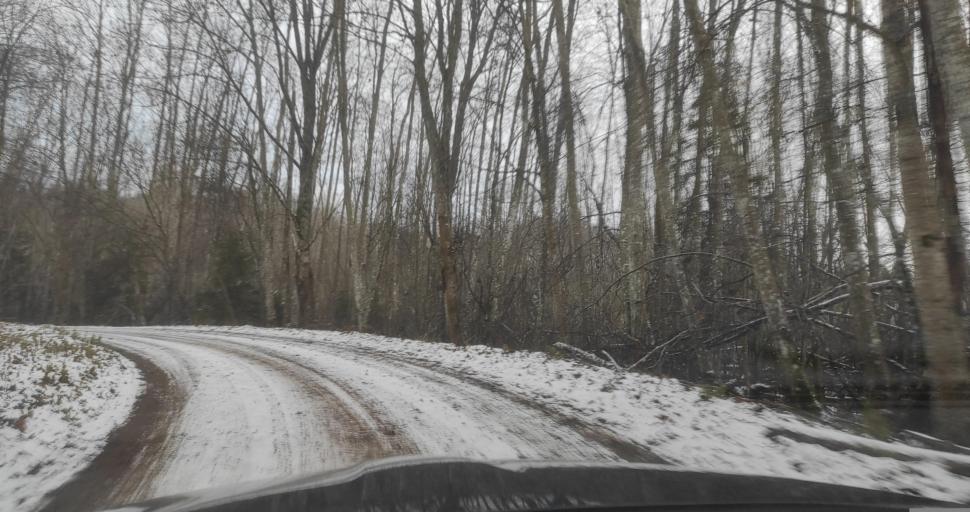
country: LV
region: Alsunga
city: Alsunga
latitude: 56.9570
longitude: 21.6451
